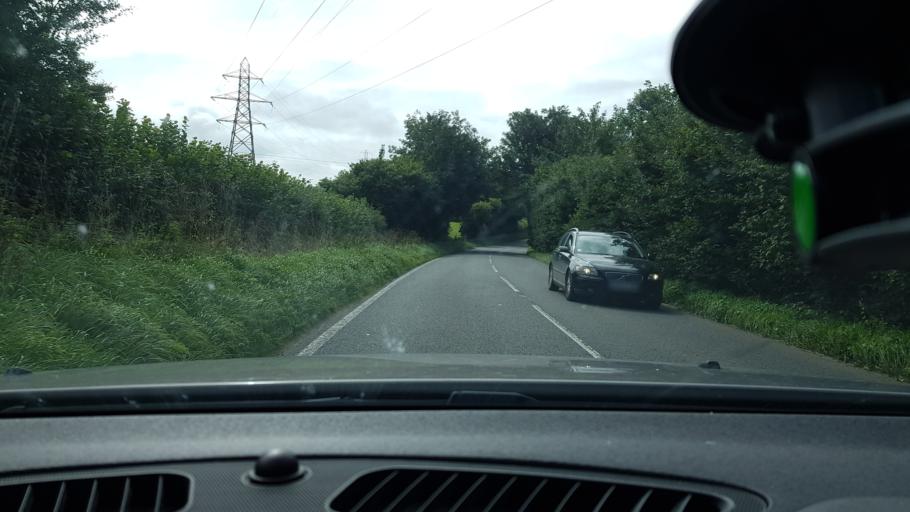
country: GB
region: England
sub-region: Cornwall
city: Camelford
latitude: 50.6030
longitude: -4.6959
